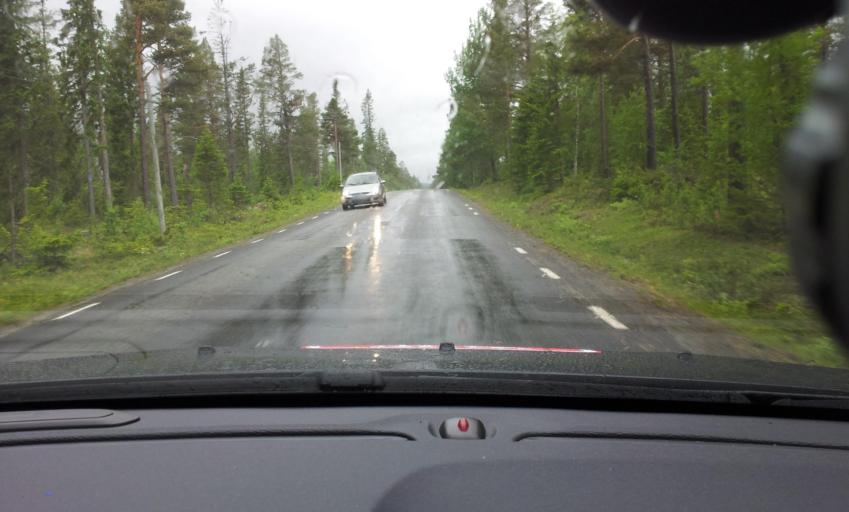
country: SE
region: Jaemtland
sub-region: Are Kommun
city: Are
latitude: 63.1818
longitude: 13.1154
